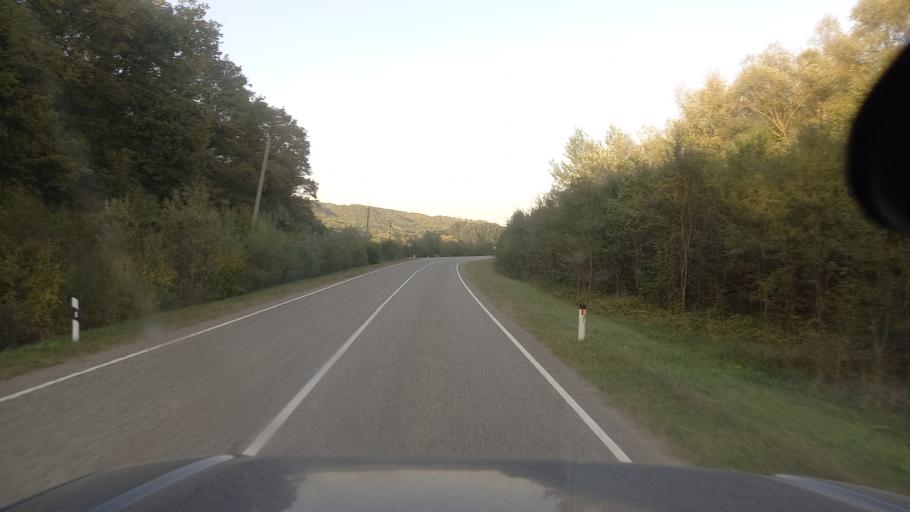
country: RU
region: Krasnodarskiy
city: Smolenskaya
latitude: 44.7367
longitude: 38.7264
